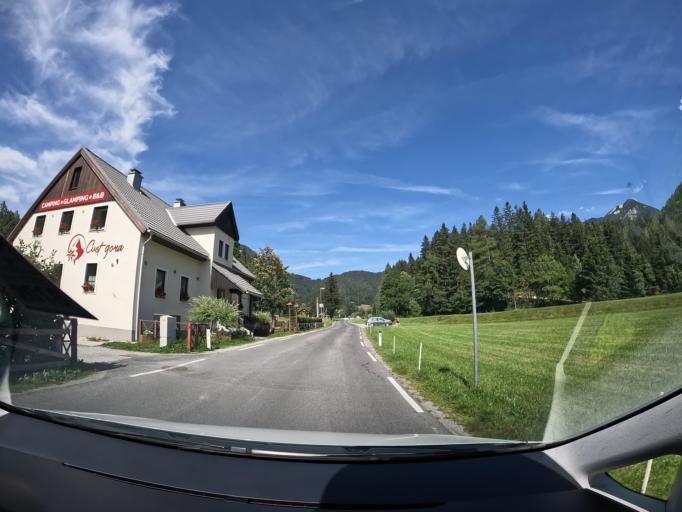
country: AT
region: Carinthia
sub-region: Politischer Bezirk Feldkirchen
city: Feldkirchen in Karnten
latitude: 46.7046
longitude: 14.1244
